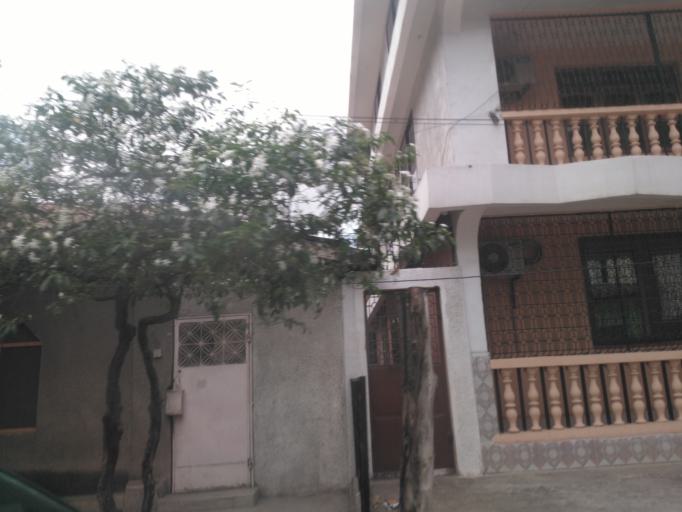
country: TZ
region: Dar es Salaam
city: Dar es Salaam
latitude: -6.8138
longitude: 39.2720
